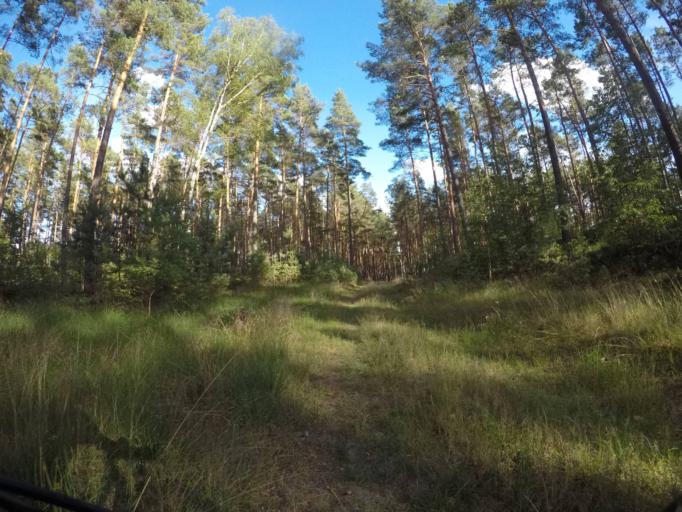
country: DE
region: Mecklenburg-Vorpommern
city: Lubtheen
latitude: 53.2476
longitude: 11.0091
